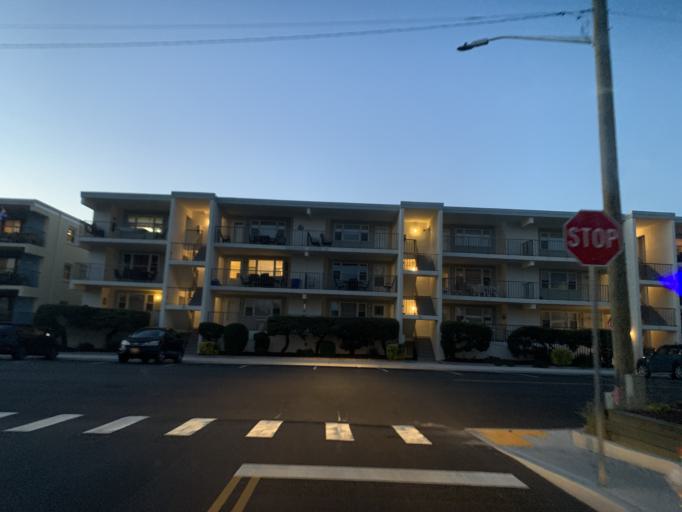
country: US
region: Maryland
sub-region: Worcester County
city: Ocean City
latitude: 38.4351
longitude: -75.0533
